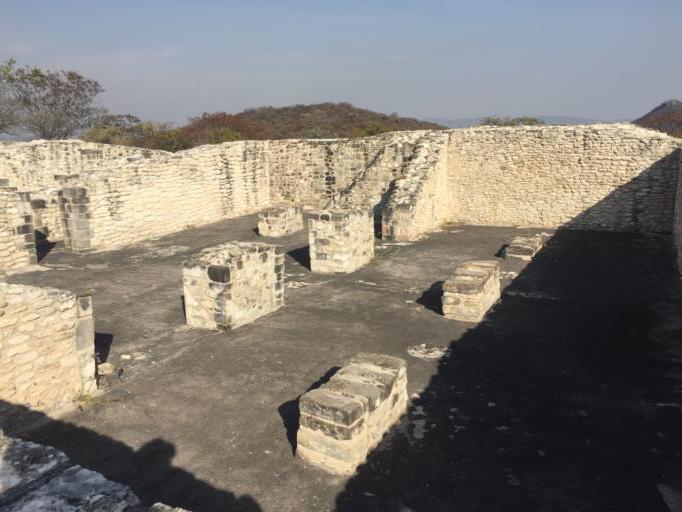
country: MX
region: Morelos
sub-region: Miacatlan
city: Xochicalco (Cirenio Longares)
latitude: 18.8046
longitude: -99.2977
